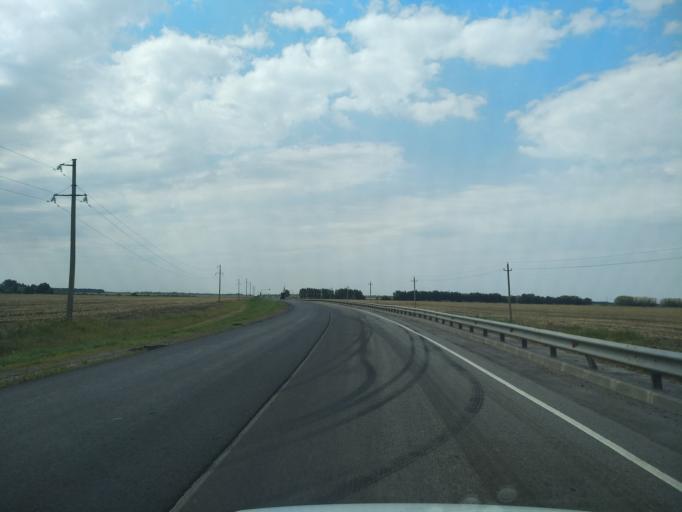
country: RU
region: Voronezj
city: Pereleshino
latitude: 51.8000
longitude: 40.1528
